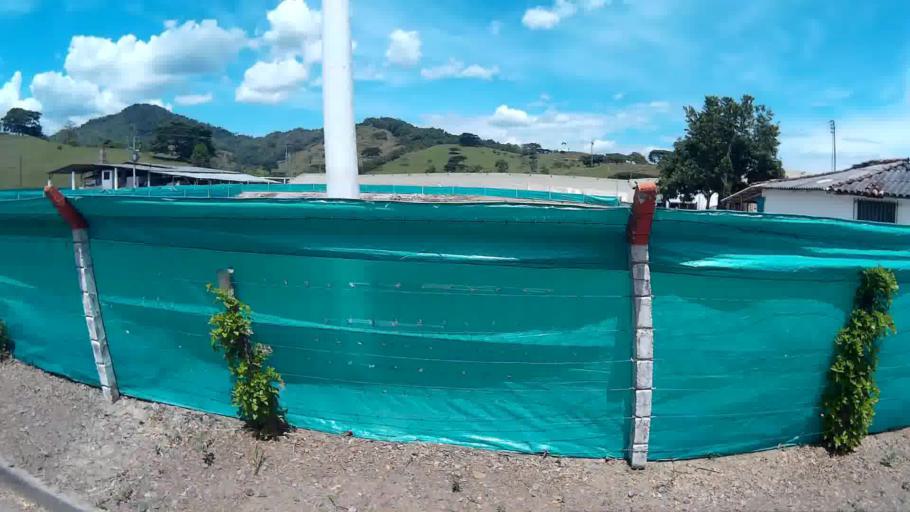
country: CO
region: Risaralda
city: La Virginia
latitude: 4.9354
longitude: -75.8595
